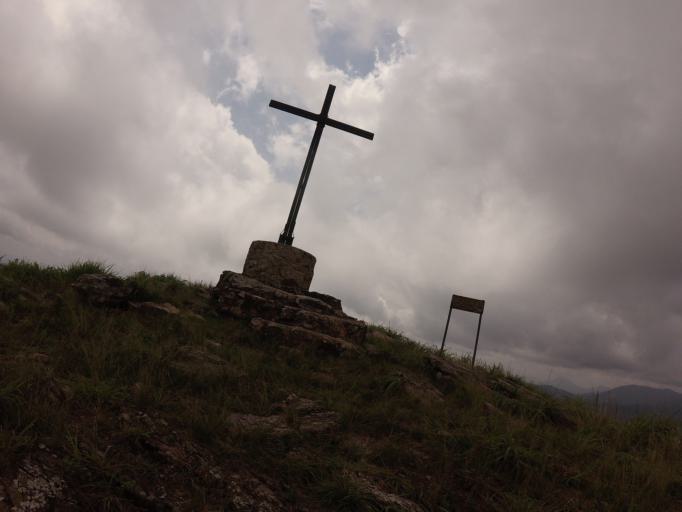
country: GH
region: Volta
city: Kpandu
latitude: 6.8556
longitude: 0.4335
